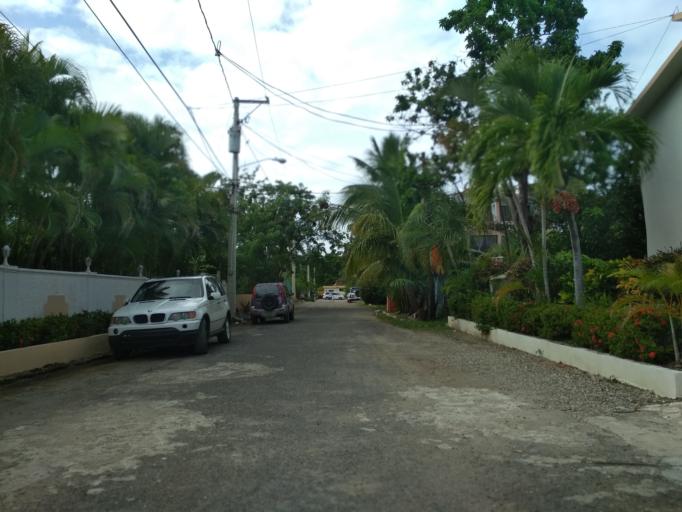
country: DO
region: Puerto Plata
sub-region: Puerto Plata
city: Puerto Plata
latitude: 19.8135
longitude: -70.7141
